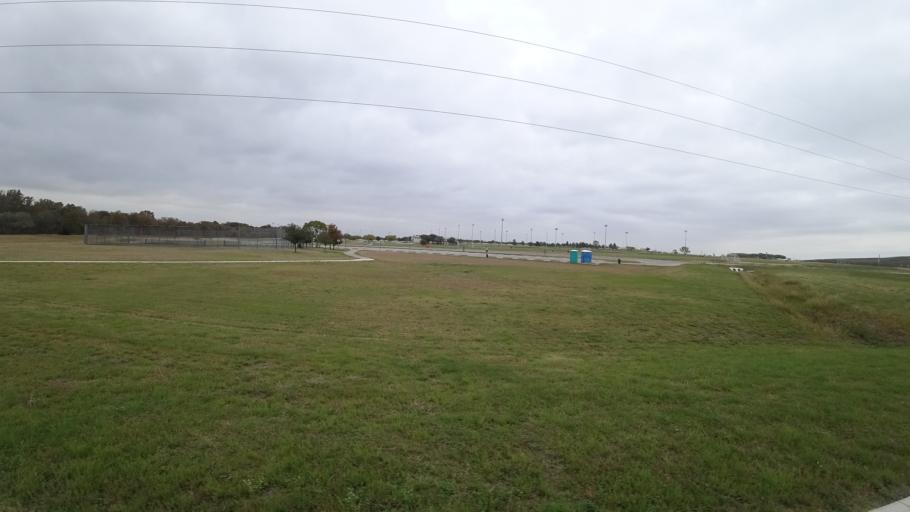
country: US
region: Texas
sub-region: Travis County
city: Pflugerville
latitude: 30.4087
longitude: -97.5985
